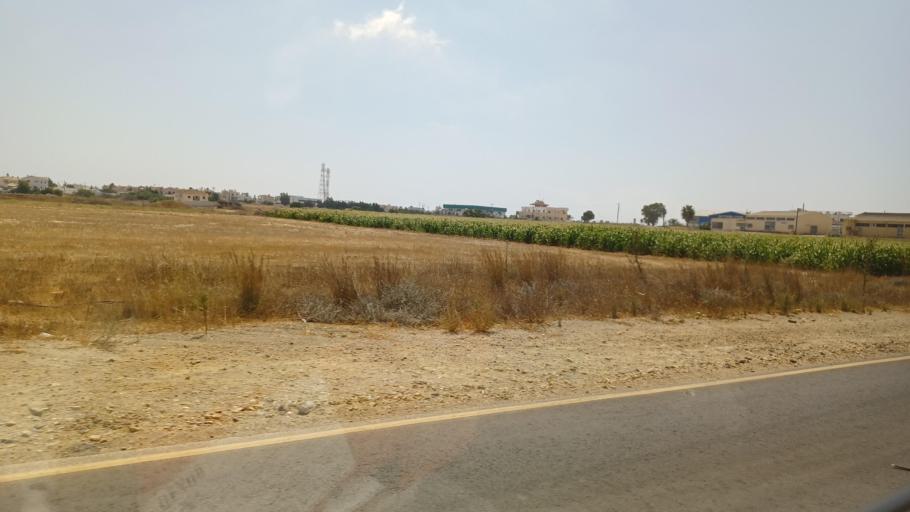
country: CY
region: Ammochostos
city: Deryneia
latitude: 35.0545
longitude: 33.9645
